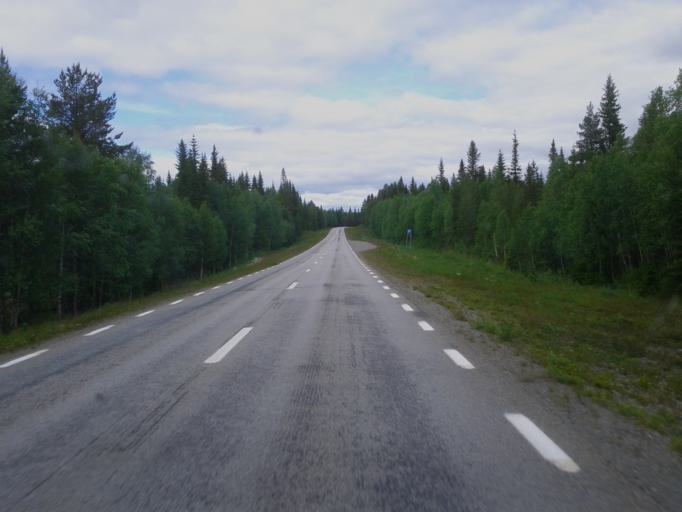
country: SE
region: Vaesterbotten
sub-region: Storumans Kommun
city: Fristad
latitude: 65.3639
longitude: 16.5280
